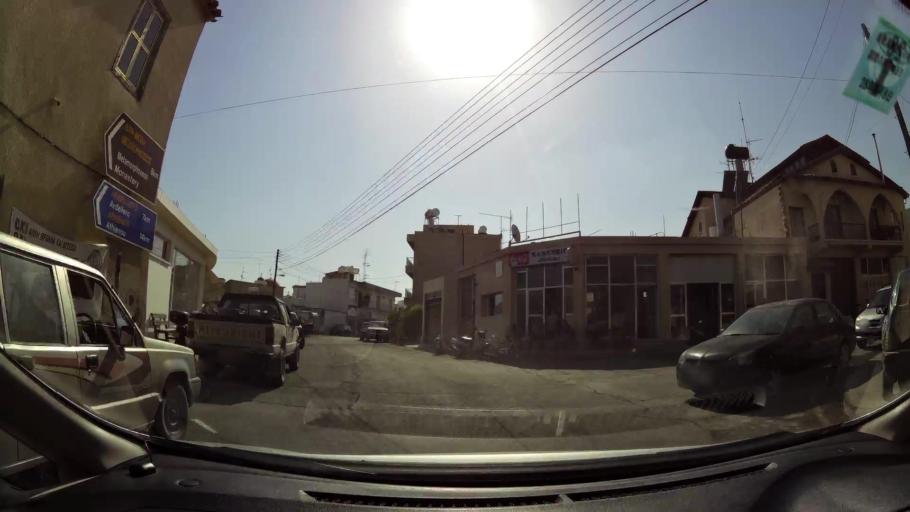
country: CY
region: Larnaka
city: Aradippou
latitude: 34.9536
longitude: 33.5896
